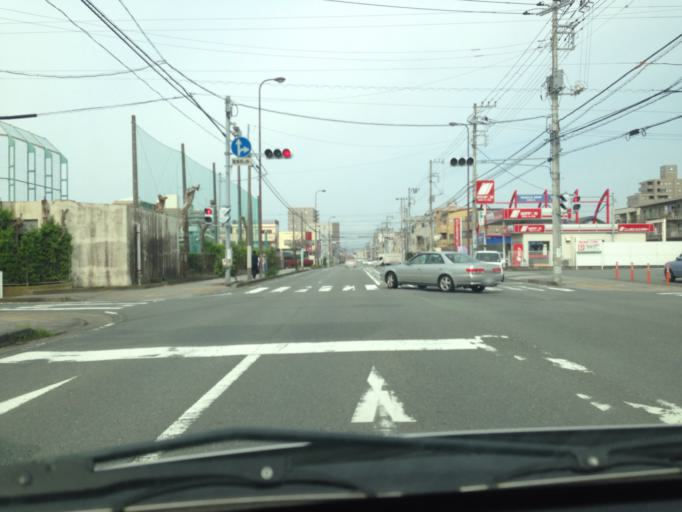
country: JP
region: Shizuoka
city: Numazu
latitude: 35.1088
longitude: 138.8649
